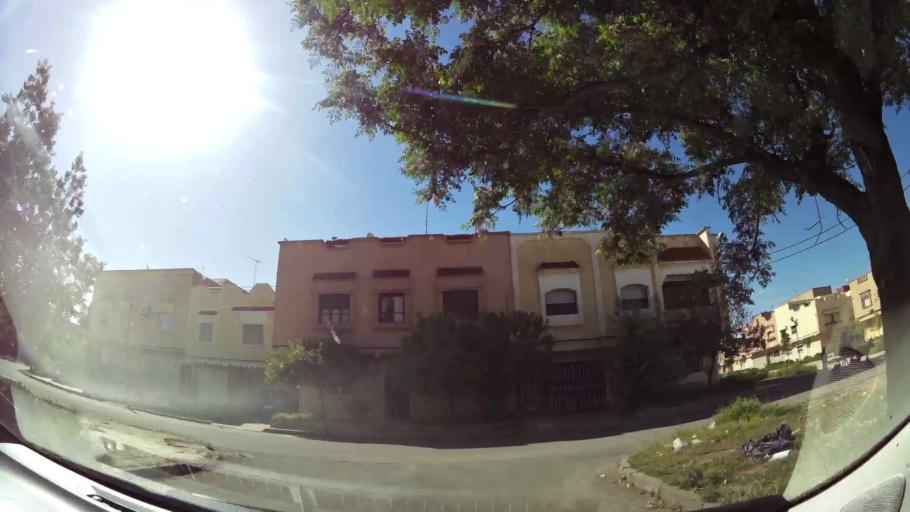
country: MA
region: Oriental
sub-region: Oujda-Angad
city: Oujda
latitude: 34.6577
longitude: -1.8950
